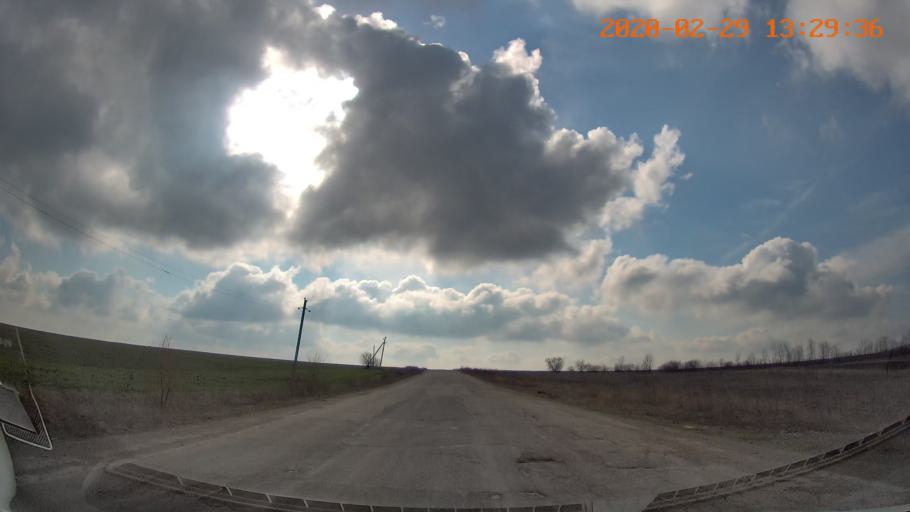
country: MD
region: Telenesti
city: Camenca
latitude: 47.8953
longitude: 28.6354
